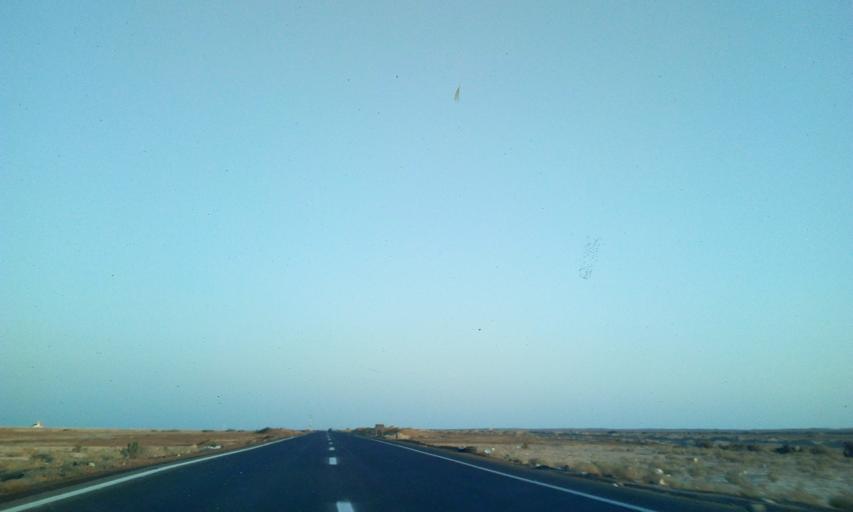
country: EG
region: South Sinai
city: Tor
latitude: 27.8211
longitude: 33.4551
